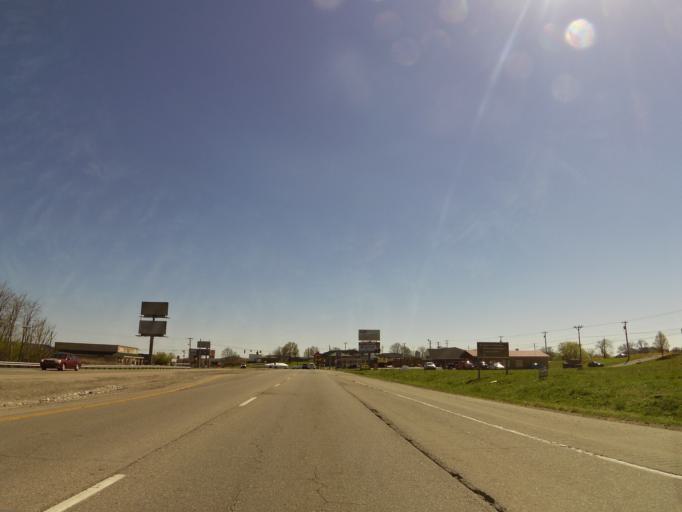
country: US
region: Kentucky
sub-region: Pulaski County
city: Somerset
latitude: 37.0191
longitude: -84.6276
